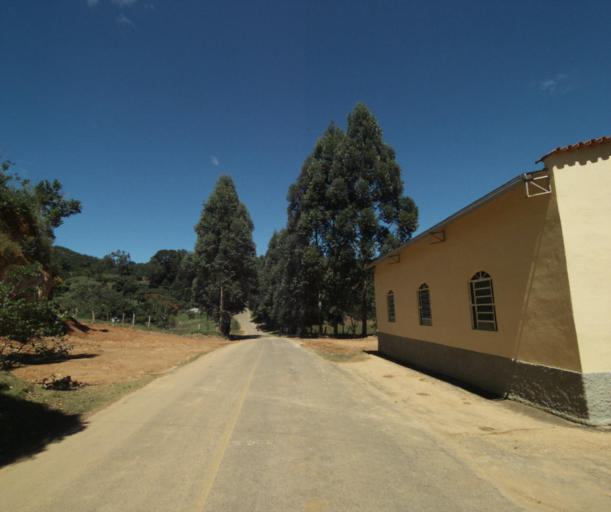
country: BR
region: Minas Gerais
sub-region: Espera Feliz
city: Espera Feliz
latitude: -20.6041
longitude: -41.8331
